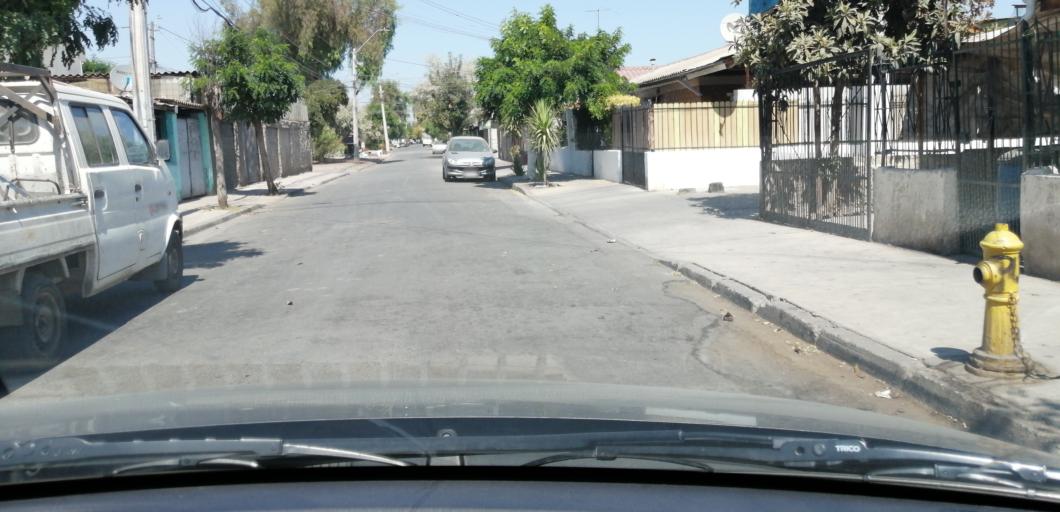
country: CL
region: Santiago Metropolitan
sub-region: Provincia de Santiago
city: Lo Prado
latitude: -33.4312
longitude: -70.7442
